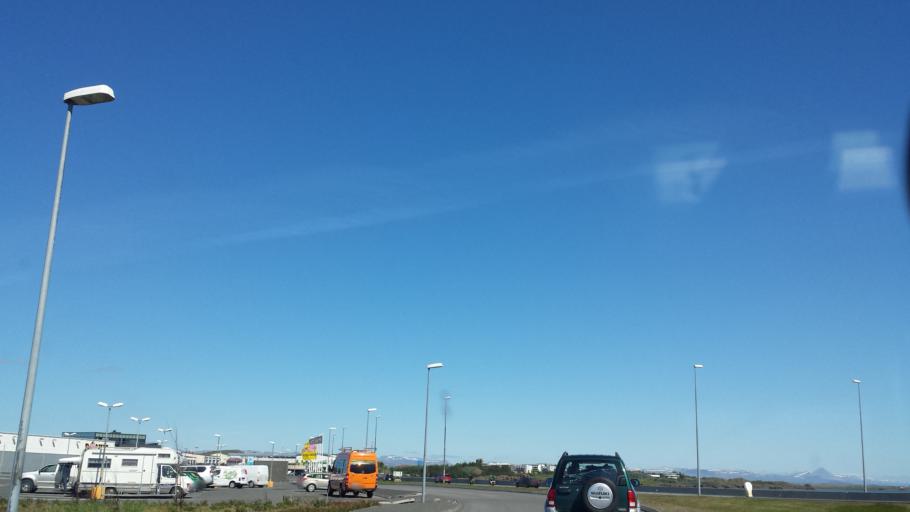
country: IS
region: West
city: Borgarnes
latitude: 64.5403
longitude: -21.9083
